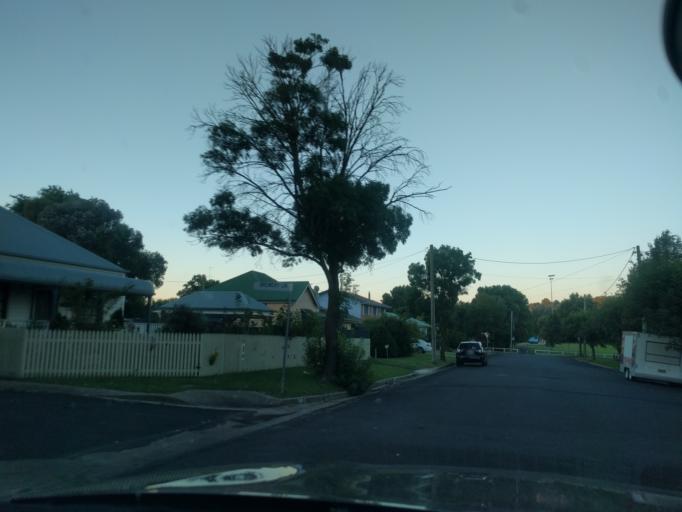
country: AU
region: New South Wales
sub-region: Armidale Dumaresq
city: Armidale
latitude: -30.5101
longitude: 151.6572
